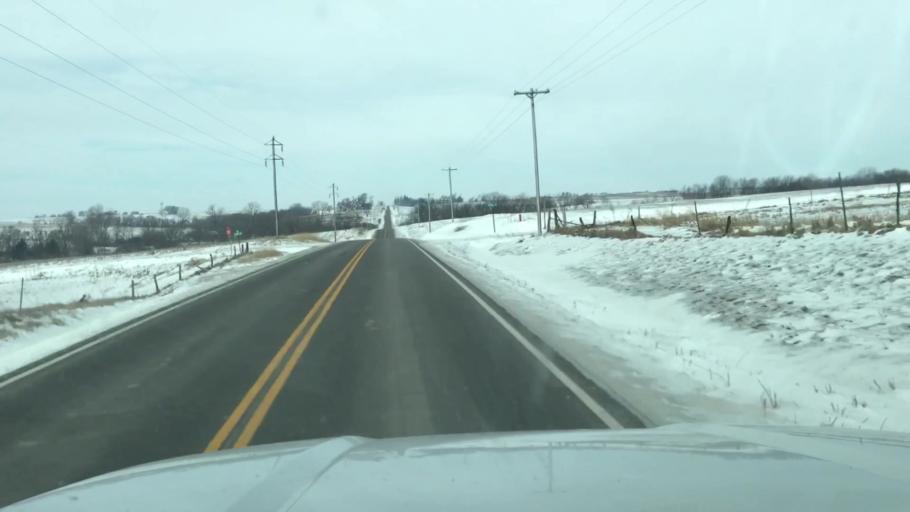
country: US
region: Missouri
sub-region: Holt County
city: Mound City
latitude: 40.1301
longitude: -95.1069
